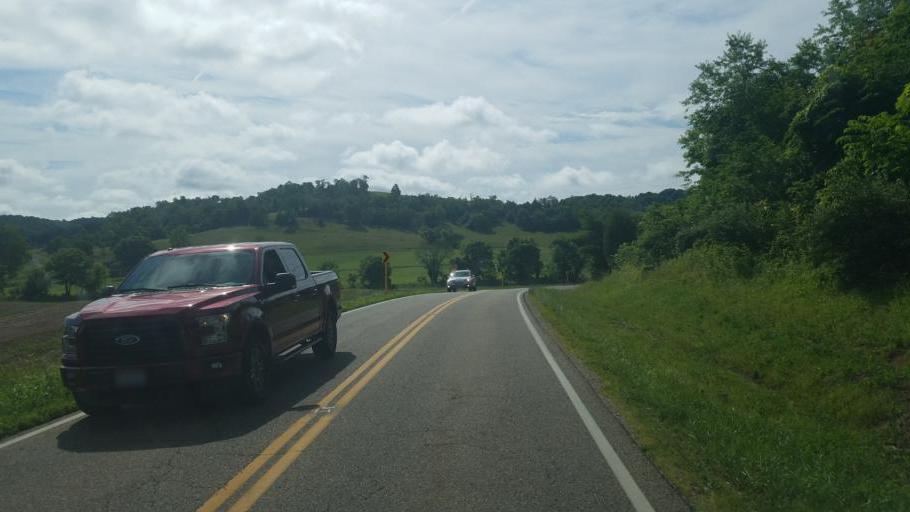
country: US
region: Ohio
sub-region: Gallia County
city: Gallipolis
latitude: 38.8289
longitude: -82.2539
